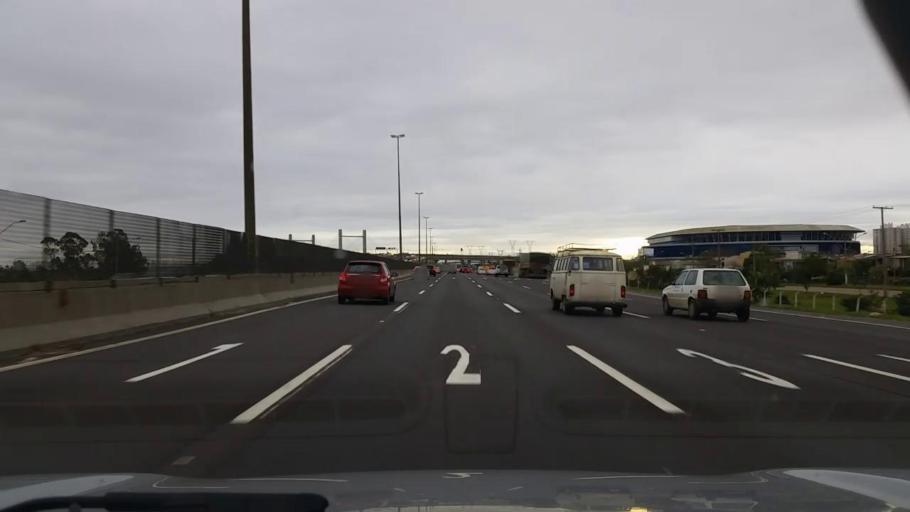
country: BR
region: Rio Grande do Sul
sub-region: Porto Alegre
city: Porto Alegre
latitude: -29.9812
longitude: -51.2012
